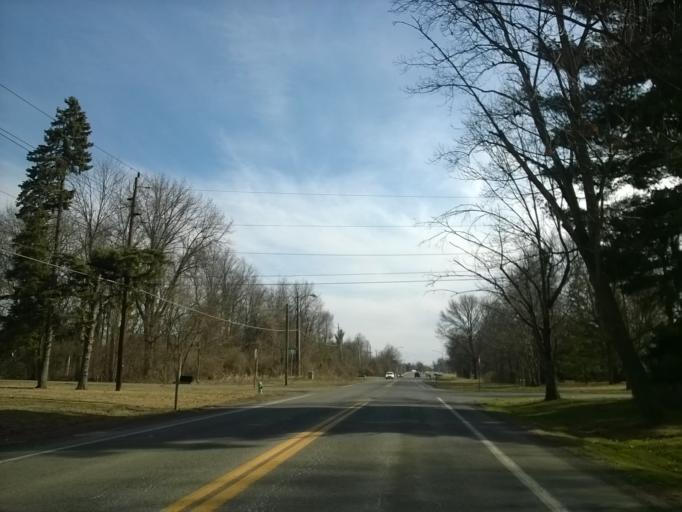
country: US
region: Indiana
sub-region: Marion County
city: Speedway
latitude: 39.8296
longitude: -86.2116
